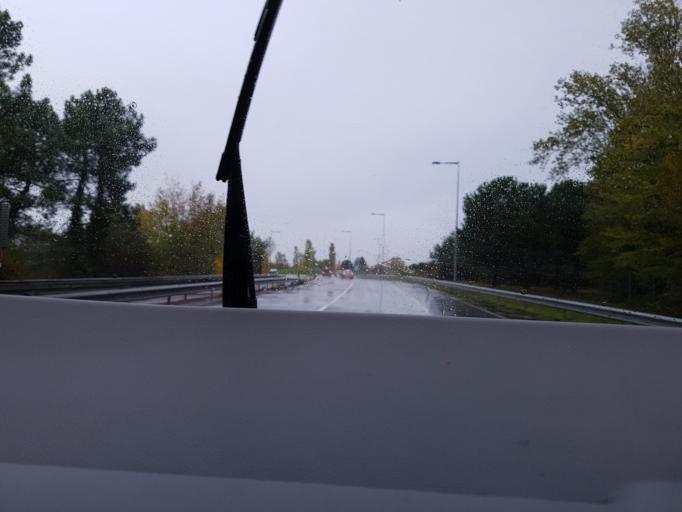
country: FR
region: Aquitaine
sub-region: Departement de la Gironde
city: Saint-Gervais
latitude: 45.0108
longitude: -0.4314
